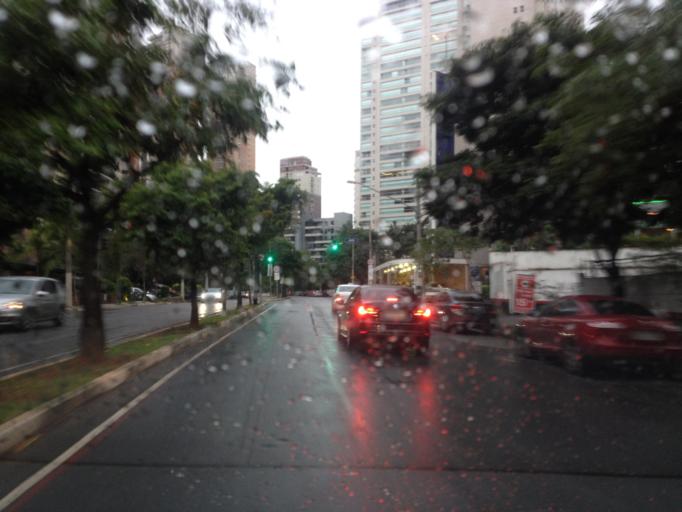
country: BR
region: Sao Paulo
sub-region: Sao Paulo
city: Sao Paulo
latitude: -23.5975
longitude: -46.6676
